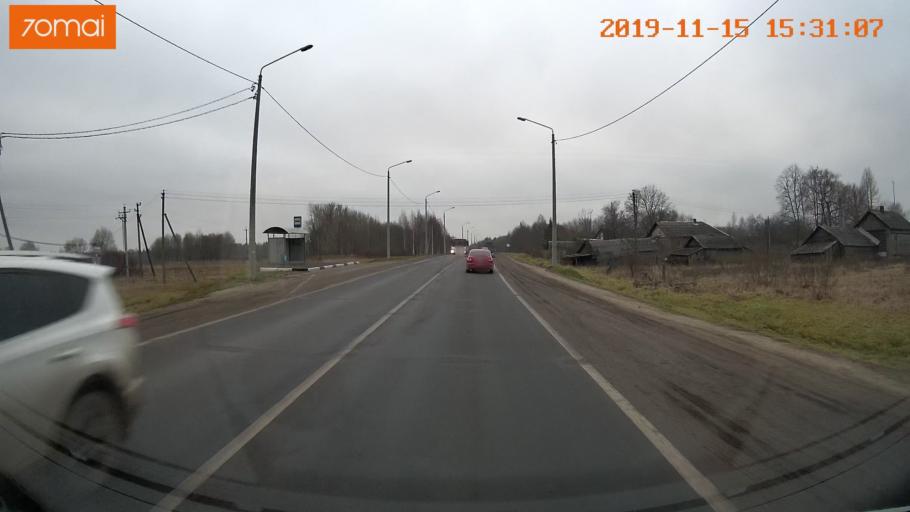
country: RU
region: Jaroslavl
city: Danilov
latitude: 58.1033
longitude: 40.1096
